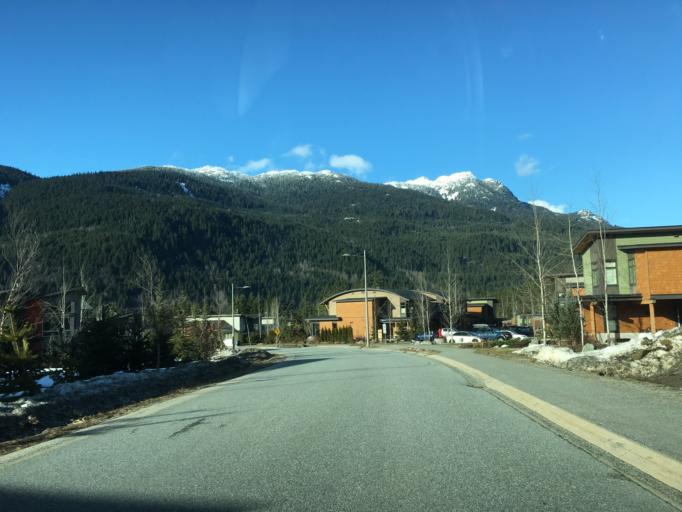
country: CA
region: British Columbia
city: Whistler
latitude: 50.0781
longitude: -123.0389
